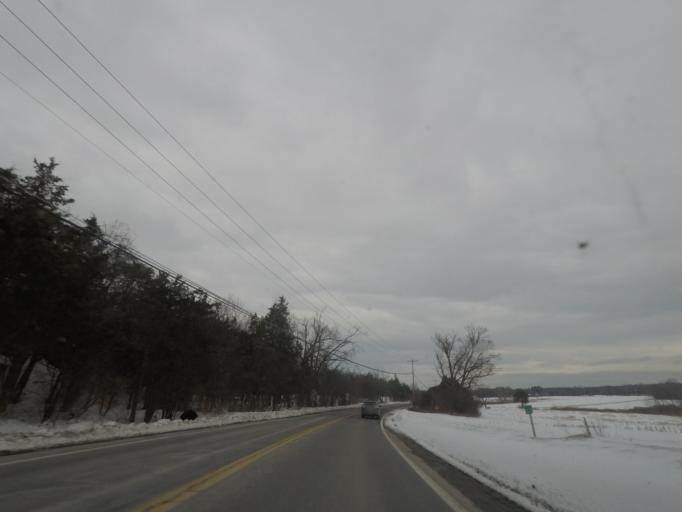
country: US
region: New York
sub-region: Columbia County
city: Kinderhook
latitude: 42.3731
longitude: -73.7324
